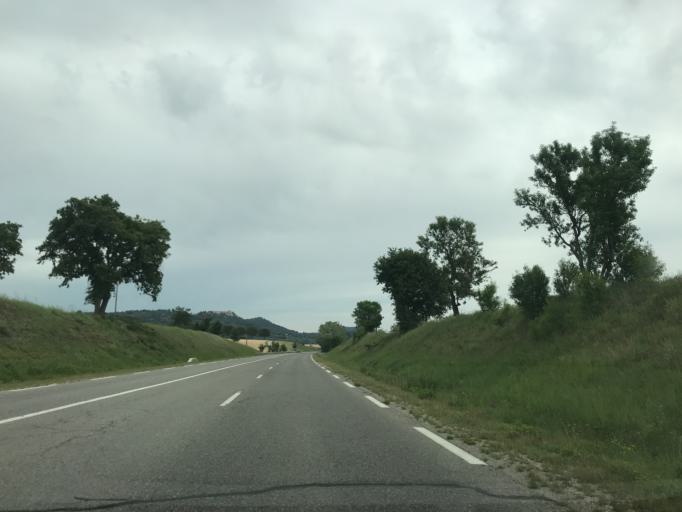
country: FR
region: Provence-Alpes-Cote d'Azur
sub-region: Departement des Alpes-de-Haute-Provence
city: Oraison
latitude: 43.9457
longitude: 5.8890
